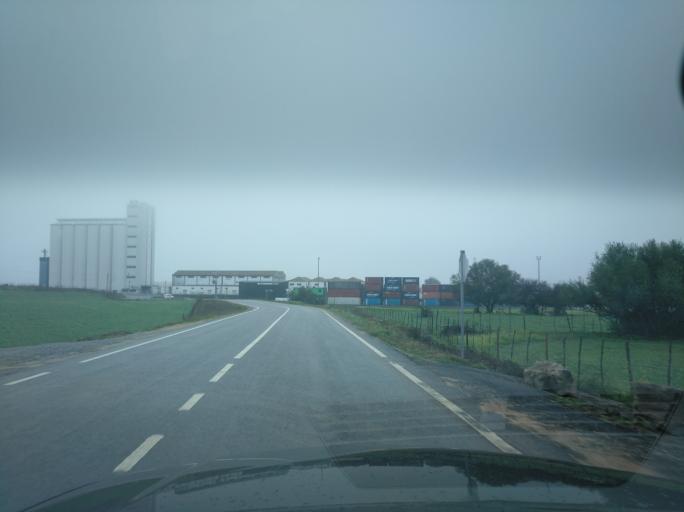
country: PT
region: Portalegre
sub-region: Elvas
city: Elvas
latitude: 38.8979
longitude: -7.1404
